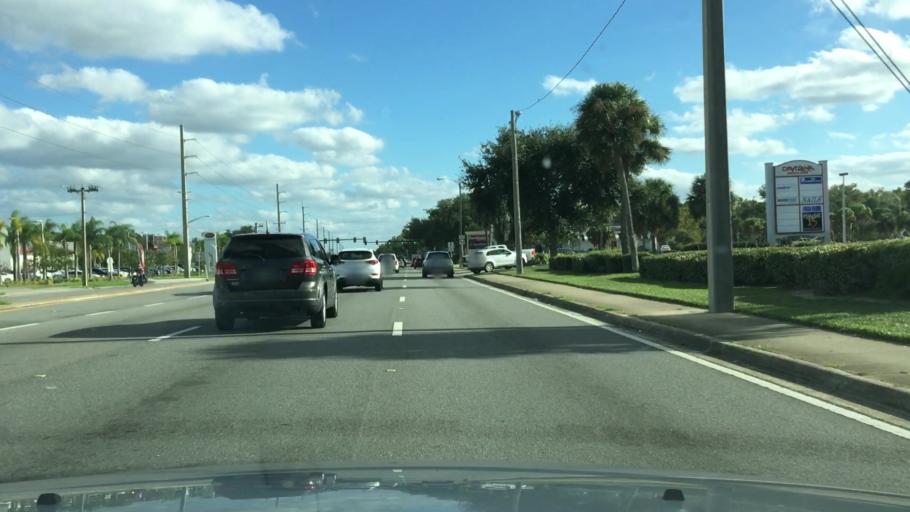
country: US
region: Florida
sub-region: Volusia County
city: Daytona Beach
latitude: 29.2053
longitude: -81.0410
